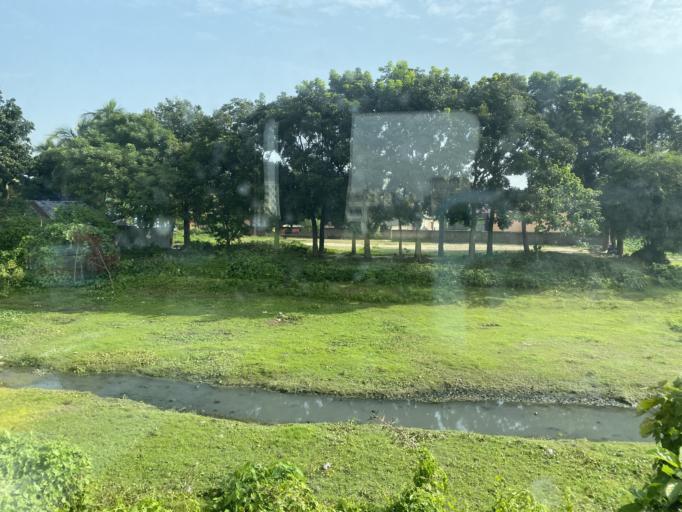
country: BD
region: Chittagong
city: Nabinagar
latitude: 23.9622
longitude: 91.1181
